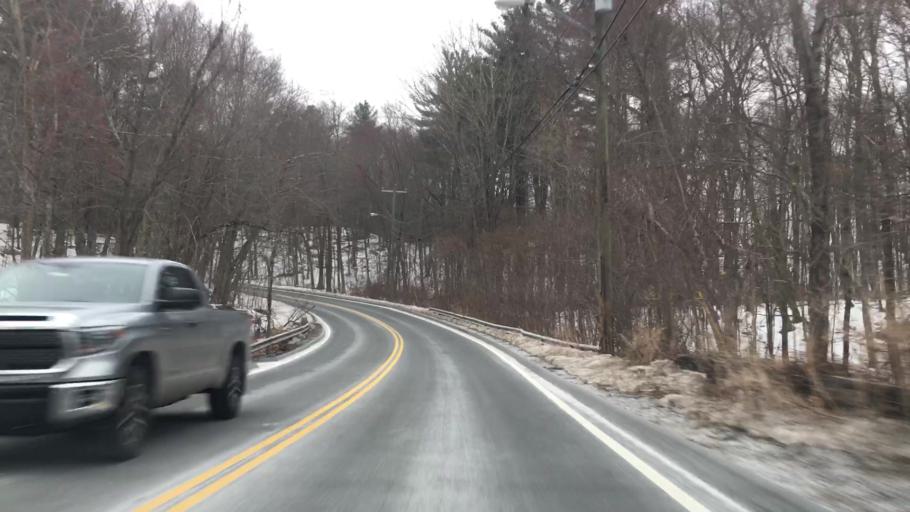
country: US
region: Massachusetts
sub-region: Hampden County
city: West Springfield
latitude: 42.0972
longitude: -72.6828
